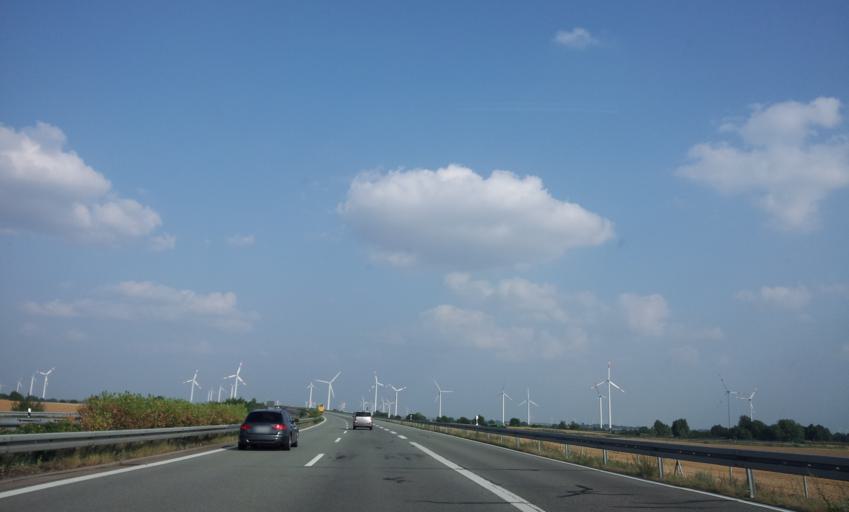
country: DE
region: Mecklenburg-Vorpommern
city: Strasburg
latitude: 53.5199
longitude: 13.7793
